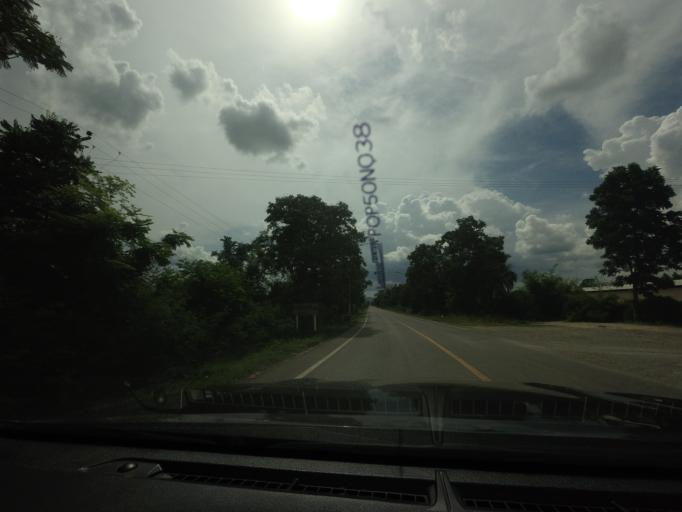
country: TH
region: Kanchanaburi
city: Bo Phloi
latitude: 14.1658
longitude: 99.4601
